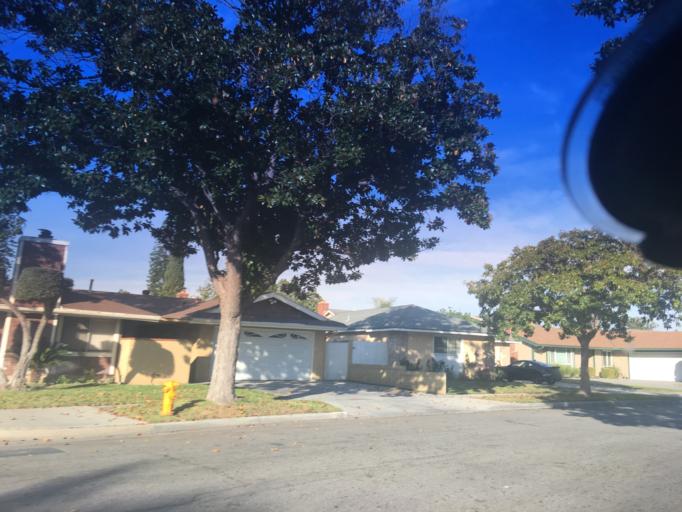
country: US
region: California
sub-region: Orange County
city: Anaheim
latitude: 33.8208
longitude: -117.8923
